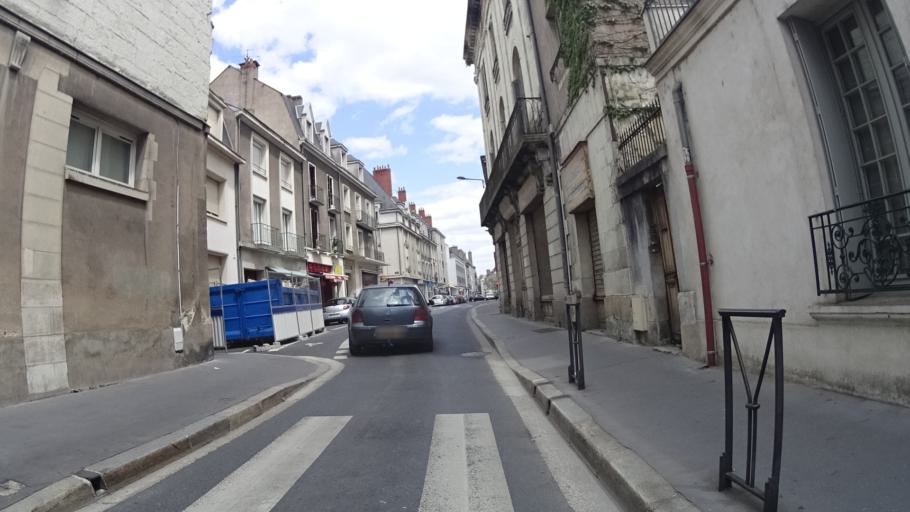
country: FR
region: Centre
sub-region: Departement d'Indre-et-Loire
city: Tours
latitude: 47.3921
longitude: 0.6840
